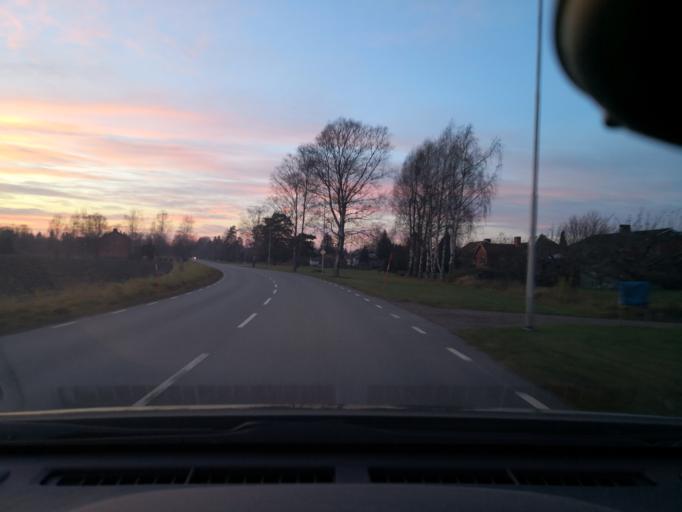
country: SE
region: OErebro
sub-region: Lindesbergs Kommun
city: Fellingsbro
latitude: 59.4300
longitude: 15.5899
